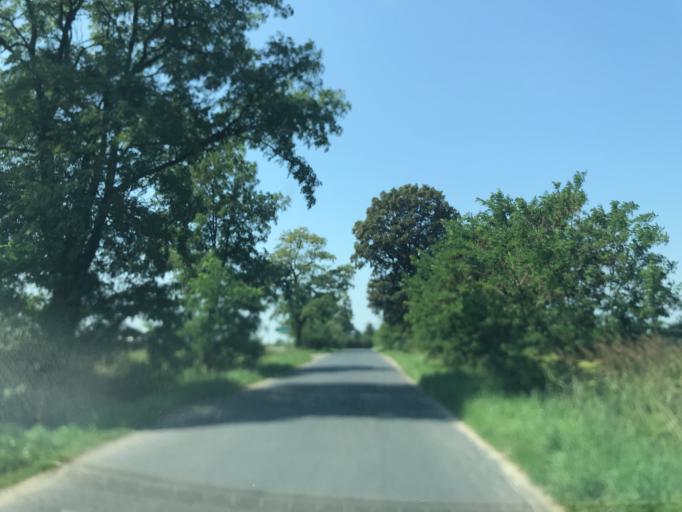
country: PL
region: Kujawsko-Pomorskie
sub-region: Powiat lipnowski
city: Chrostkowo
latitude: 52.9900
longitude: 19.2475
